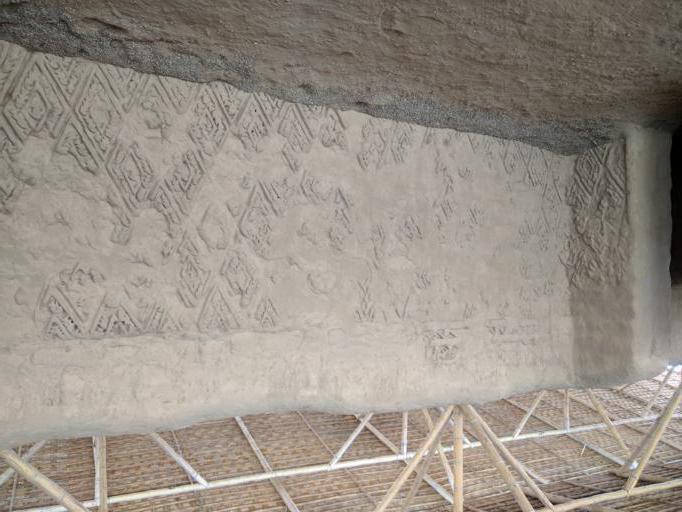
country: PE
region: La Libertad
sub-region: Provincia de Trujillo
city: Trujillo
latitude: -8.1045
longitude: -79.0450
